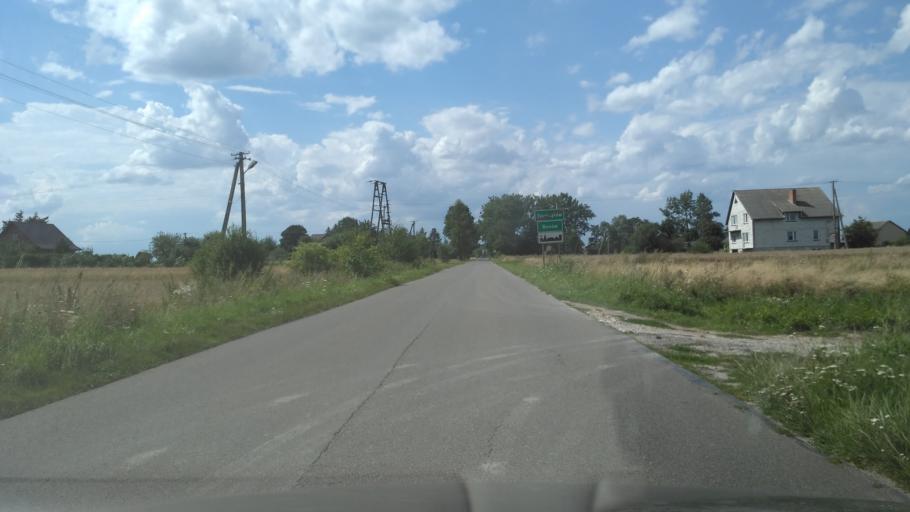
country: PL
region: Lublin Voivodeship
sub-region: Powiat leczynski
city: Milejow
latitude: 51.1827
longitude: 22.9553
